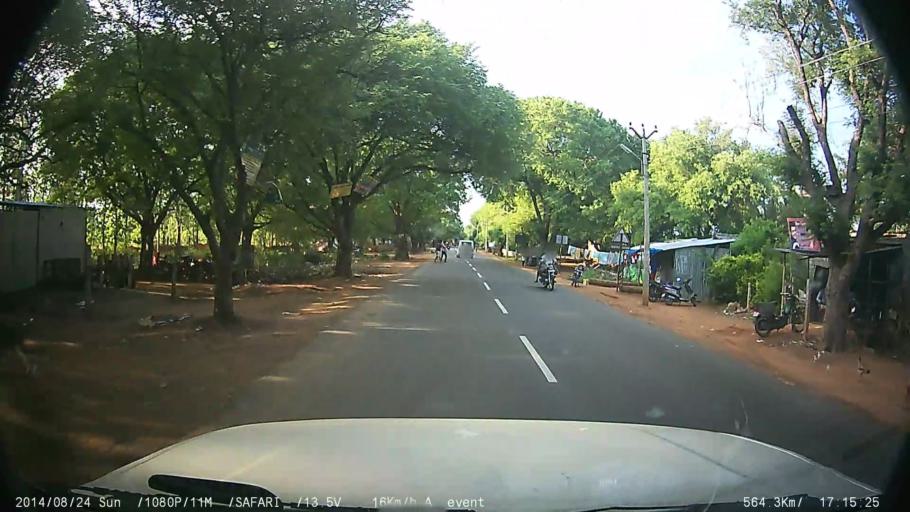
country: IN
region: Tamil Nadu
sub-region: Kancheepuram
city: Madambakkam
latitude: 12.8923
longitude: 80.0401
